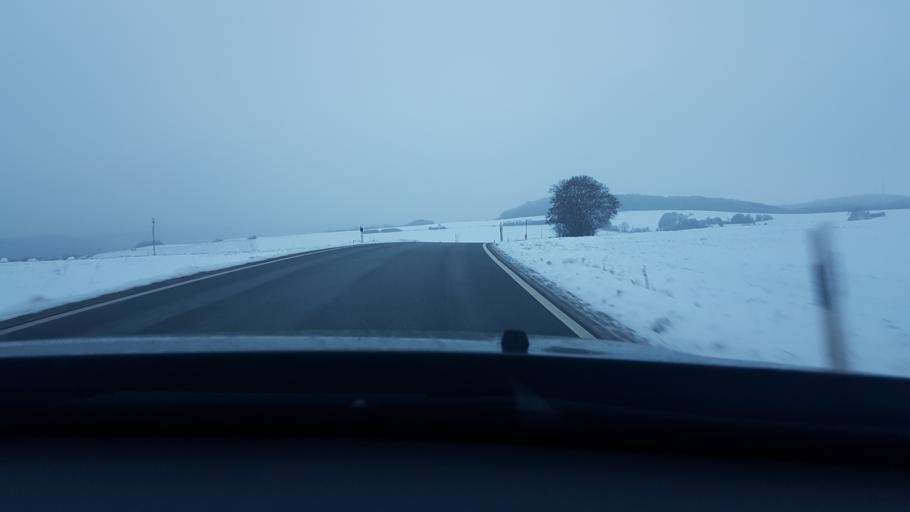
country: DE
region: Hesse
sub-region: Regierungsbezirk Kassel
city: Korbach
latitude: 51.3595
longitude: 8.8937
